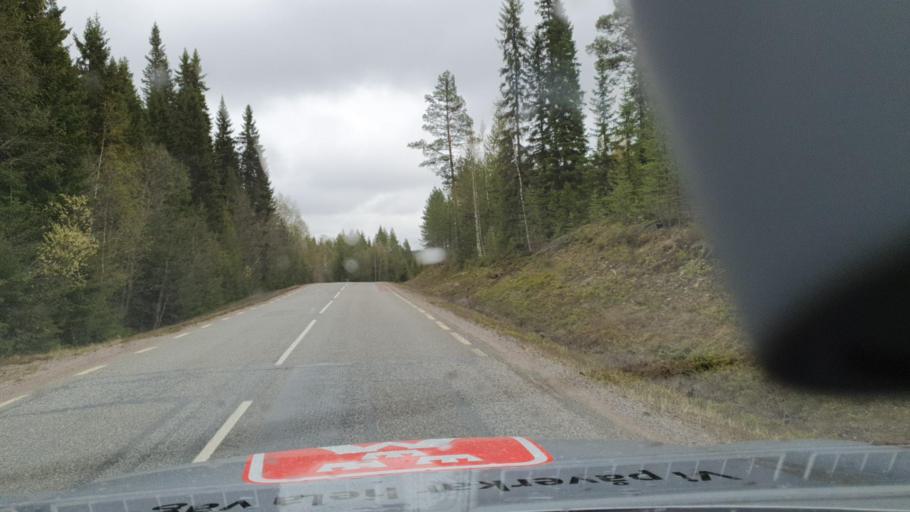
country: SE
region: Vaesterbotten
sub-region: Asele Kommun
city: Asele
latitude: 63.7045
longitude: 17.1992
